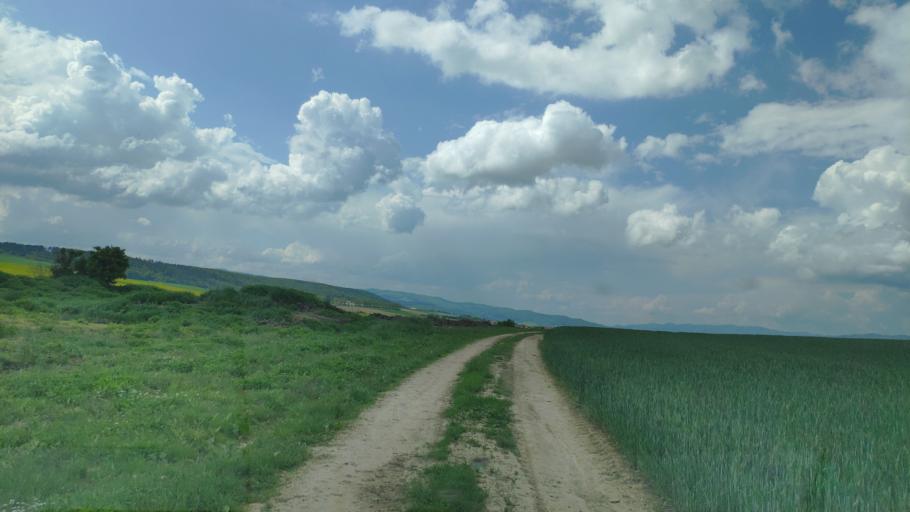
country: SK
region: Presovsky
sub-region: Okres Presov
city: Presov
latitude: 49.0296
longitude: 21.1686
